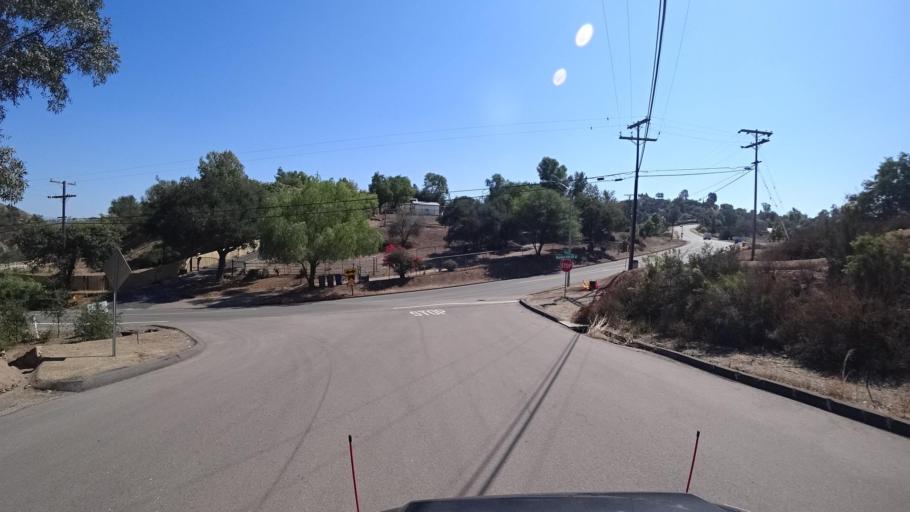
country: US
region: California
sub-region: San Diego County
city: Harbison Canyon
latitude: 32.8281
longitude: -116.8486
